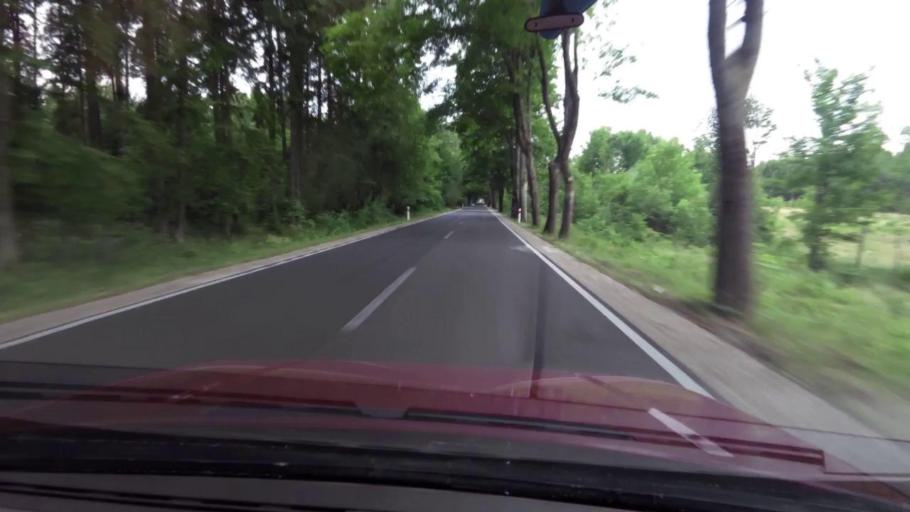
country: PL
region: West Pomeranian Voivodeship
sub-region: Powiat koszalinski
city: Sianow
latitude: 54.1530
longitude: 16.4654
